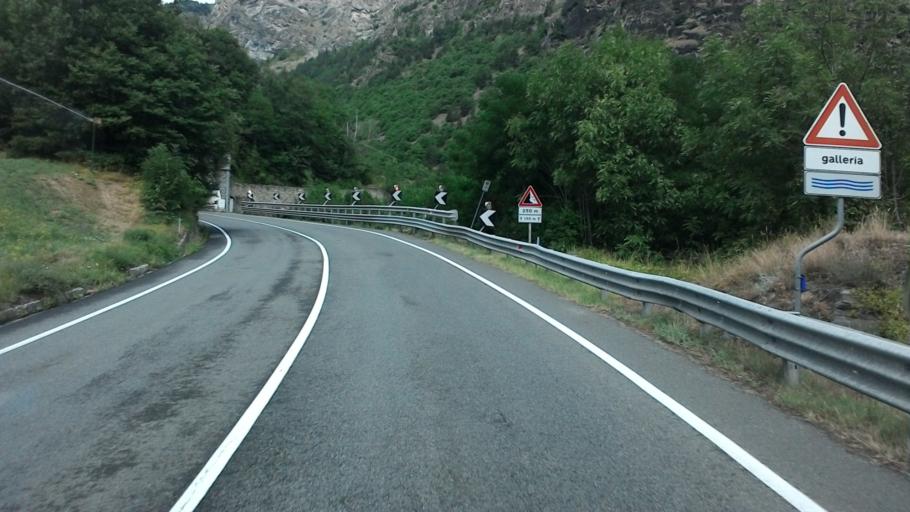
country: IT
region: Aosta Valley
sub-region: Valle d'Aosta
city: Introd
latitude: 45.7057
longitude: 7.1792
